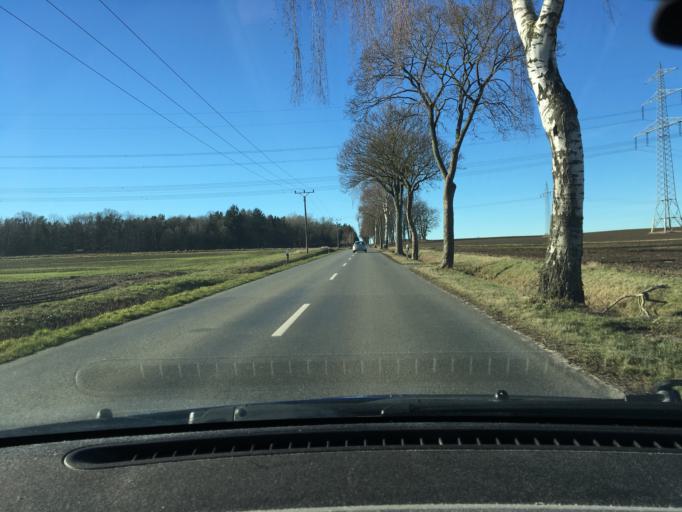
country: DE
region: Lower Saxony
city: Ebstorf
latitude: 53.0200
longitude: 10.3902
